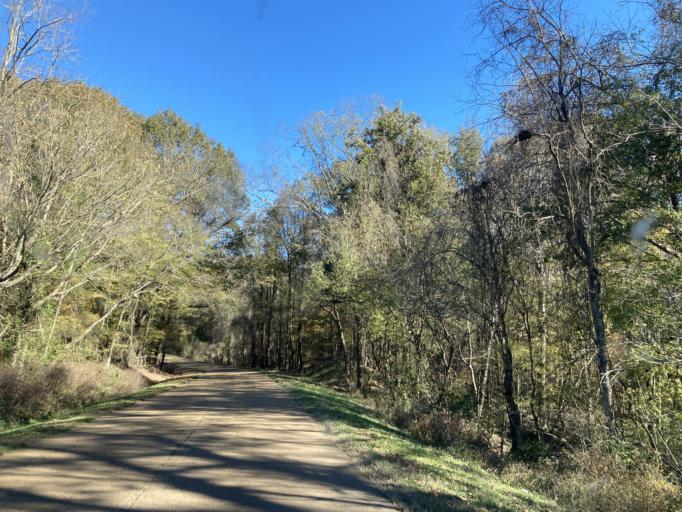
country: US
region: Mississippi
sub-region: Hinds County
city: Lynchburg
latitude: 32.5779
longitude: -90.5712
